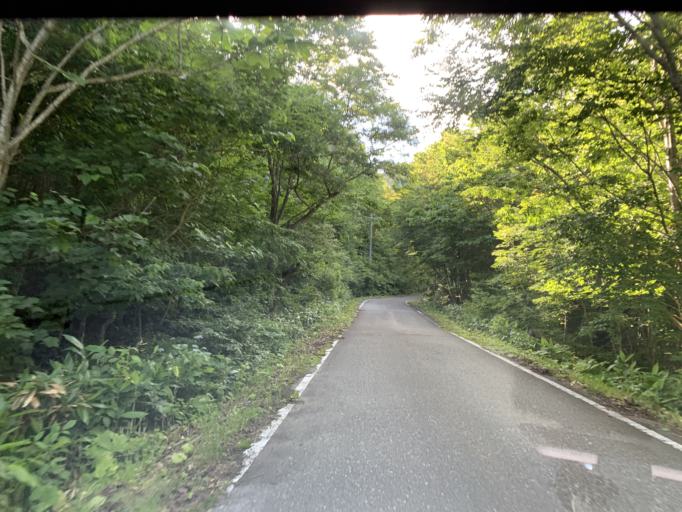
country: JP
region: Iwate
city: Ichinoseki
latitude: 38.9128
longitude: 140.8199
